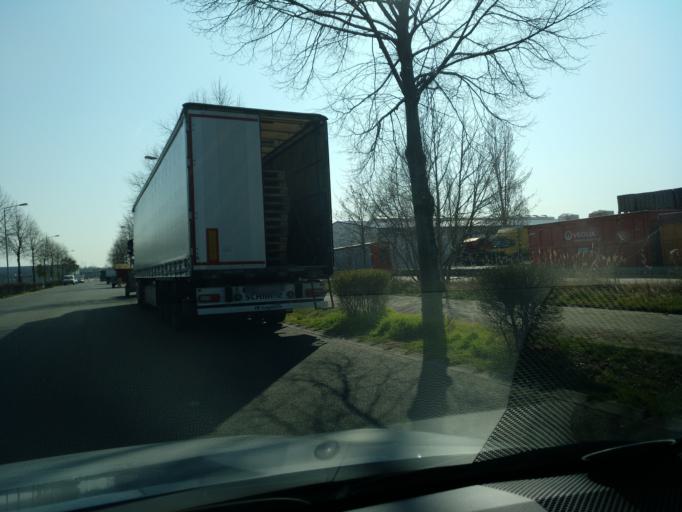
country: DE
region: Berlin
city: Mahlsdorf
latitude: 52.5044
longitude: 13.6360
